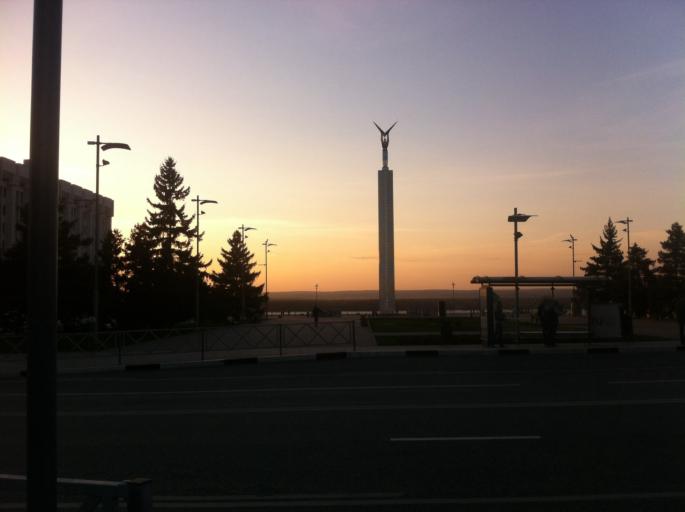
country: RU
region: Samara
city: Samara
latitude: 53.2026
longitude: 50.1114
